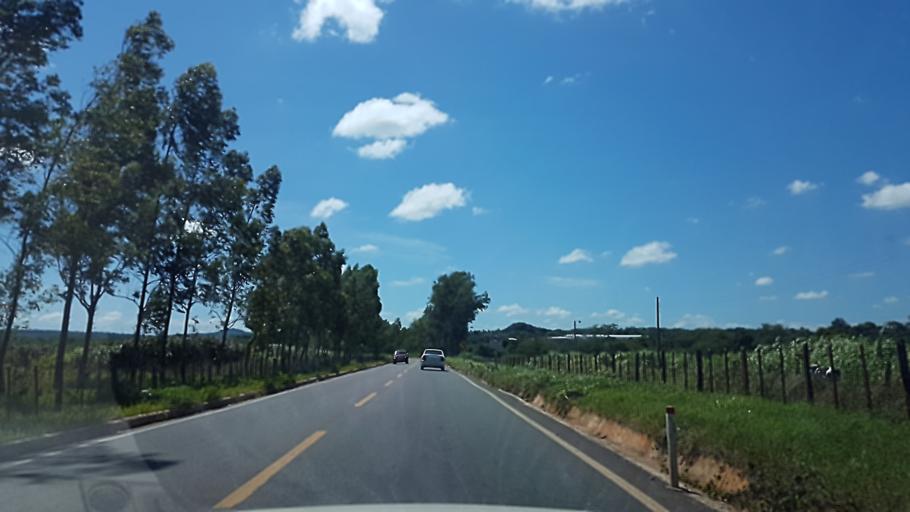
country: PY
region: Central
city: Capiata
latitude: -25.3145
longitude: -57.4602
